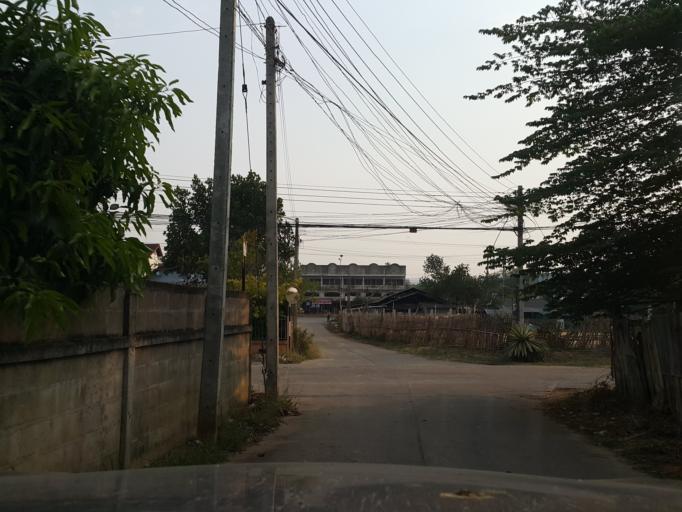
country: TH
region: Lamphun
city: Li
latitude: 17.8071
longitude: 98.9460
